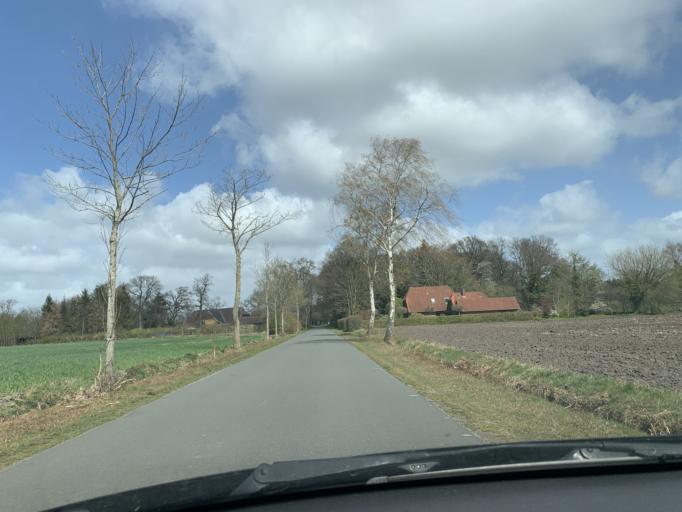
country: DE
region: Lower Saxony
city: Westerstede
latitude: 53.2804
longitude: 7.9435
